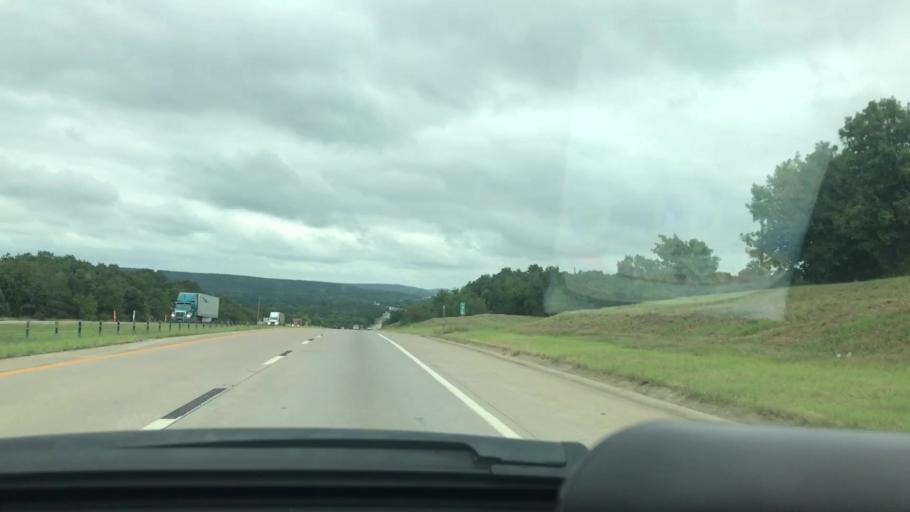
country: US
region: Oklahoma
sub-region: Pittsburg County
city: Krebs
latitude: 34.9894
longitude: -95.7218
